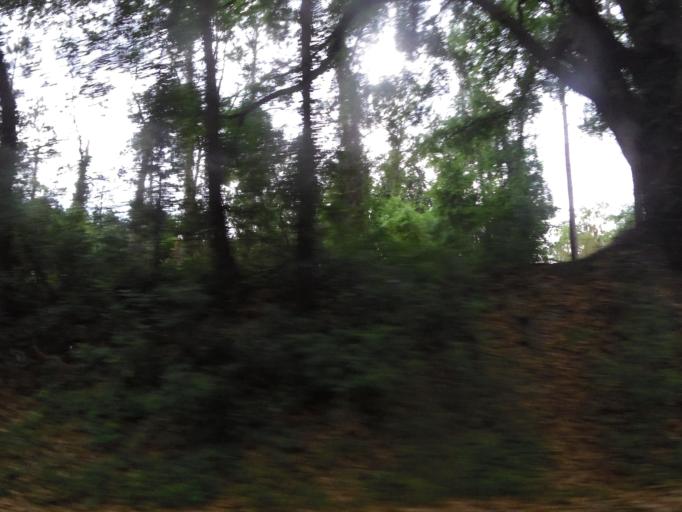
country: US
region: Florida
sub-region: Clay County
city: Bellair-Meadowbrook Terrace
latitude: 30.2007
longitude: -81.7251
